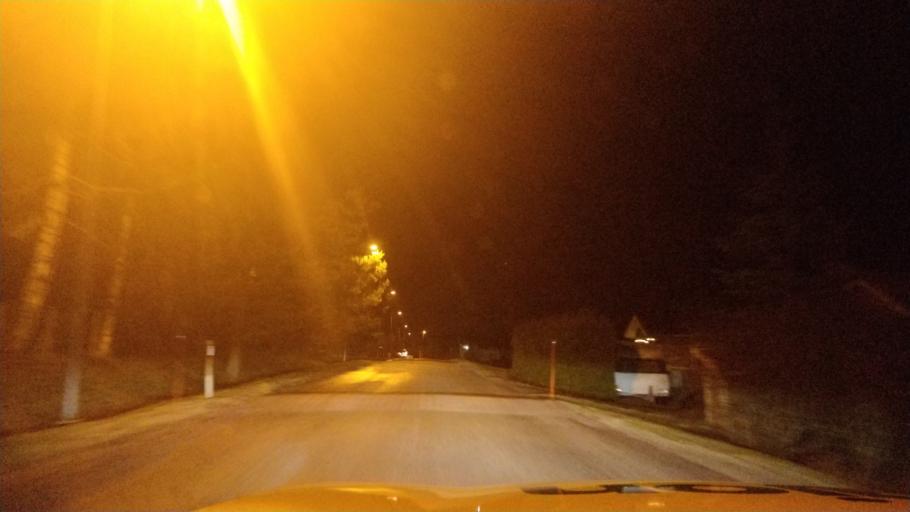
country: FI
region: Uusimaa
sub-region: Helsinki
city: Nurmijaervi
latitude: 60.3800
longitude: 24.6932
